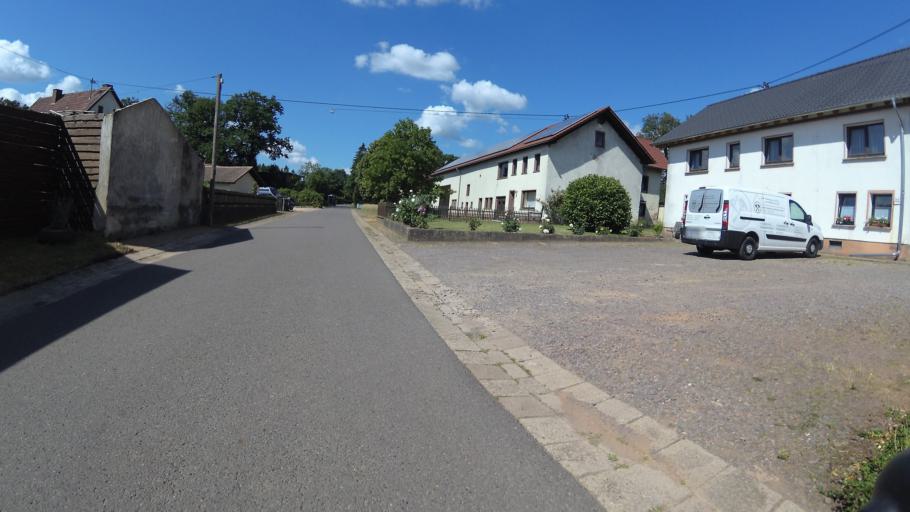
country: DE
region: Saarland
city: Weiskirchen
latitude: 49.5231
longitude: 6.8167
